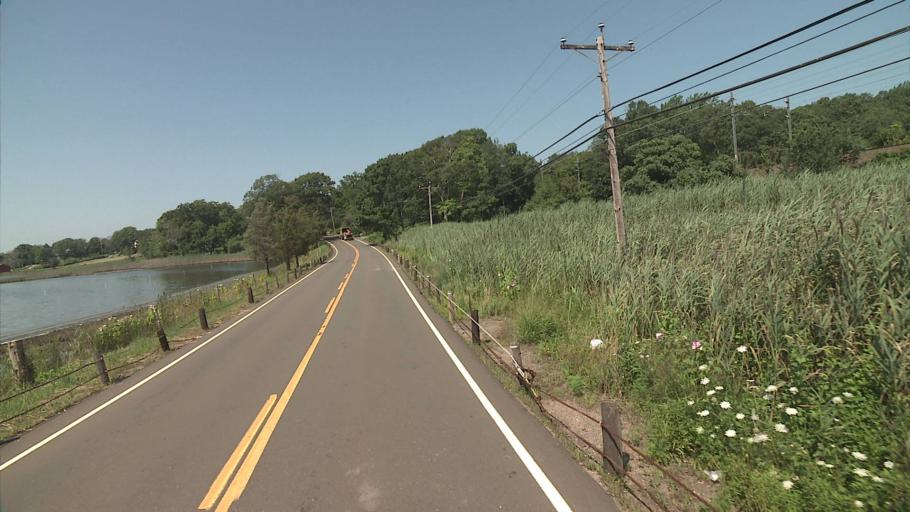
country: US
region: Connecticut
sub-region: New Haven County
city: Guilford
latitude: 41.2659
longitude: -72.7115
